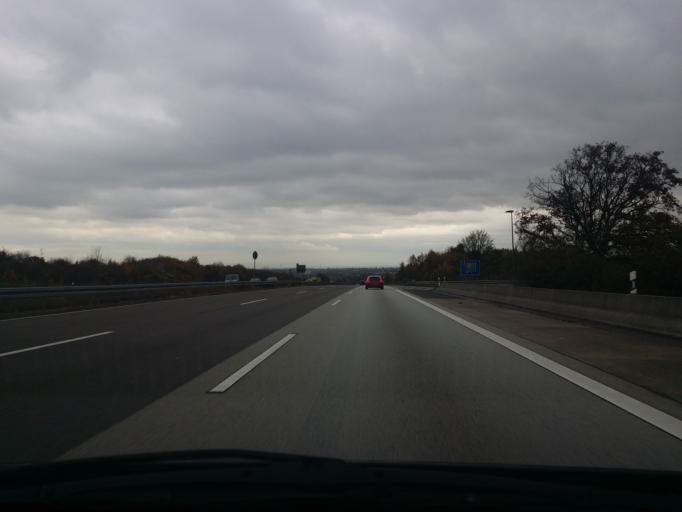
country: DE
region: Hesse
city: Eppstein
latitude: 50.0939
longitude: 8.3538
